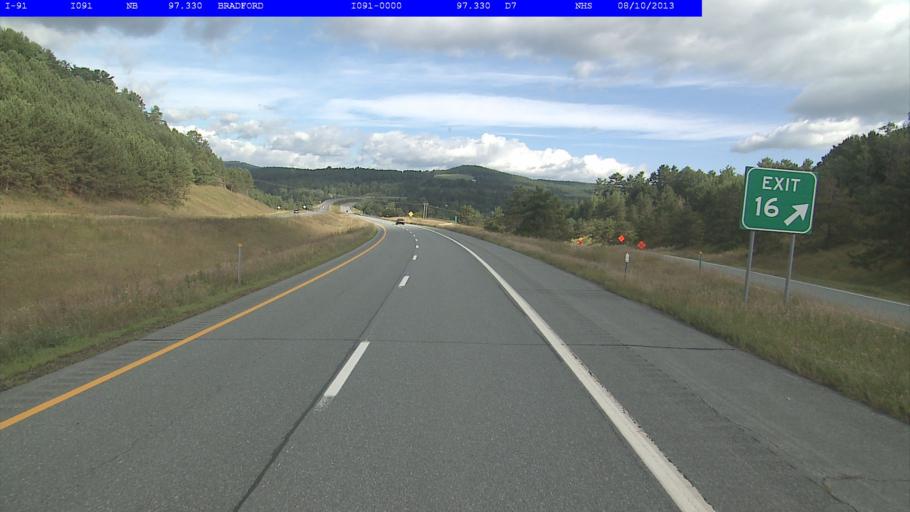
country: US
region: New Hampshire
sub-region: Grafton County
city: Orford
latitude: 43.9805
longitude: -72.1267
